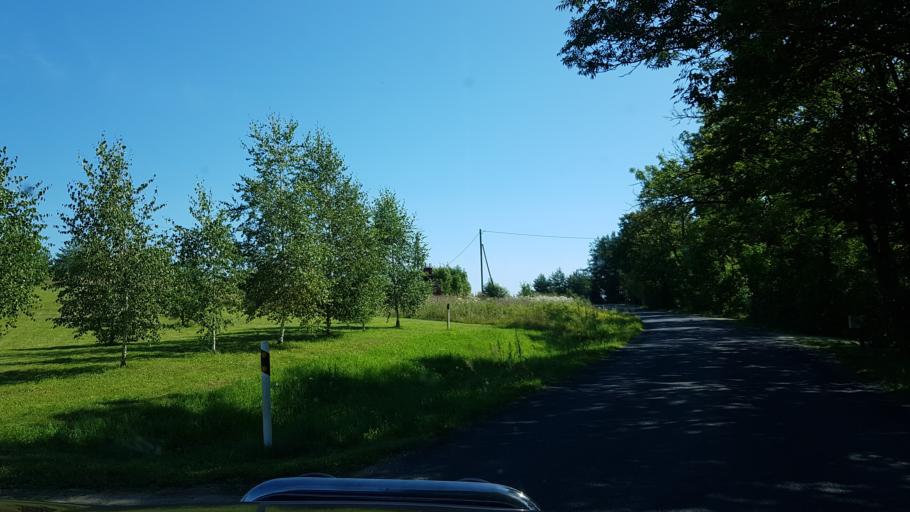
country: EE
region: Tartu
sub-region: Elva linn
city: Elva
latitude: 58.2431
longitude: 26.3992
